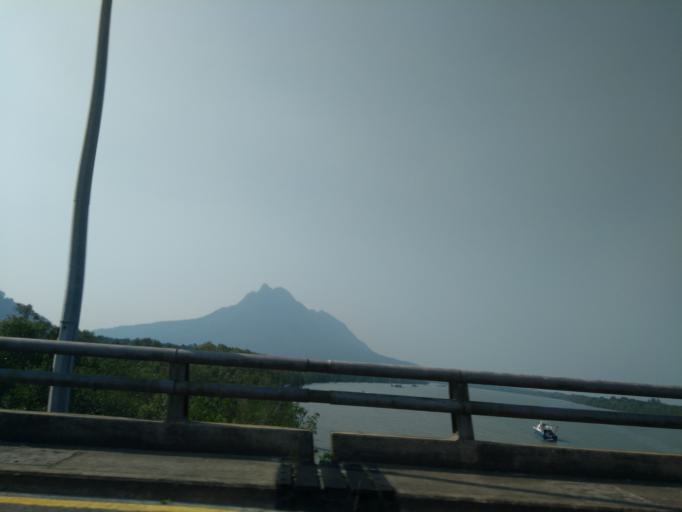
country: MY
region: Sarawak
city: Kuching
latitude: 1.6799
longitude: 110.3374
